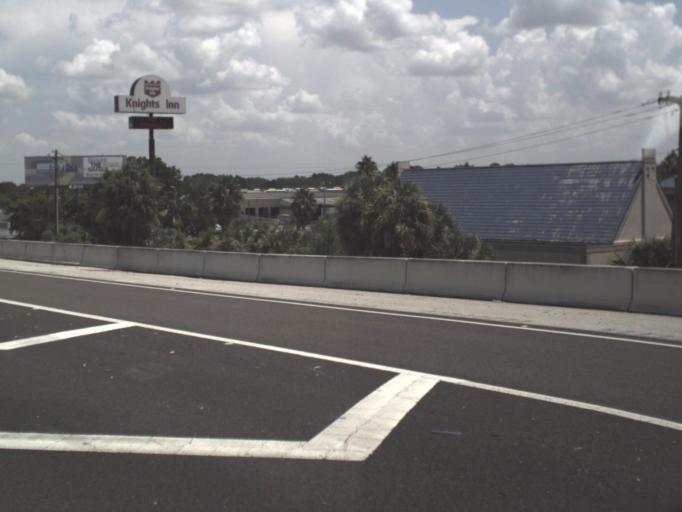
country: US
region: Florida
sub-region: Hillsborough County
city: Plant City
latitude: 28.0358
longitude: -82.1235
